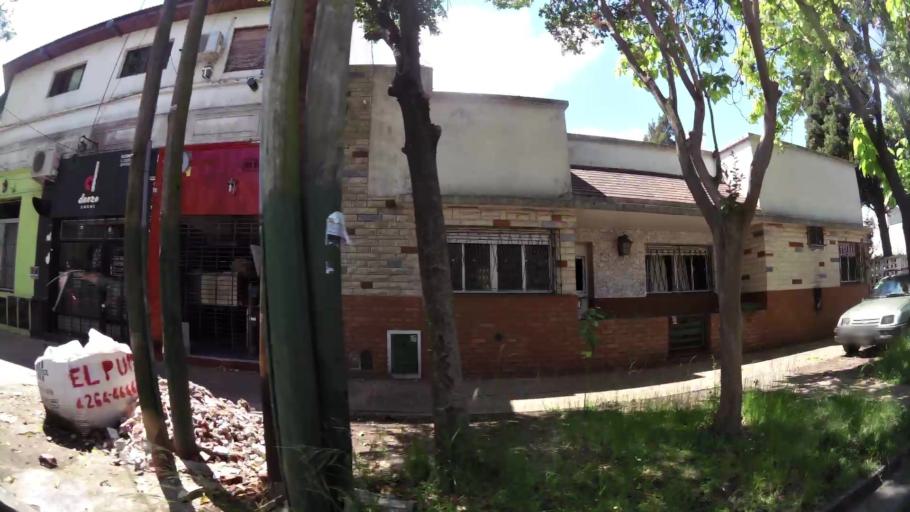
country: AR
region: Buenos Aires
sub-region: Partido de Lomas de Zamora
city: Lomas de Zamora
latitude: -34.7416
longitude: -58.4059
